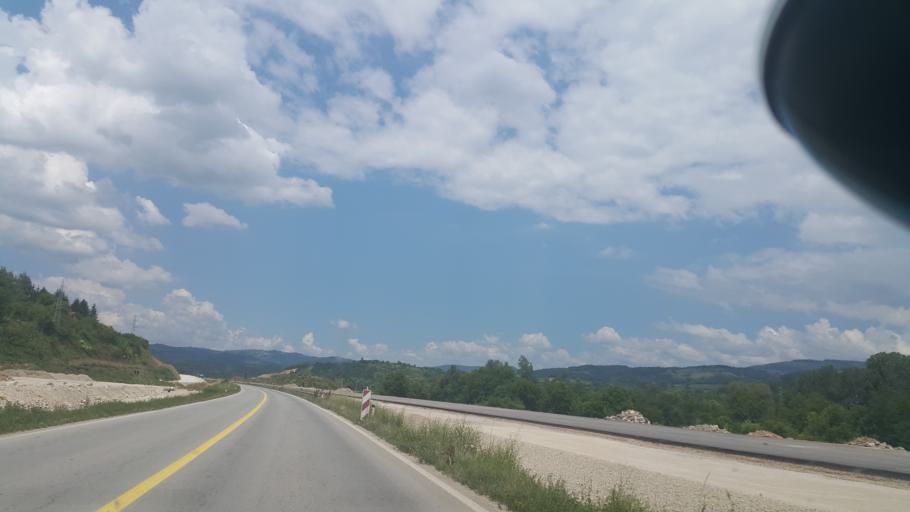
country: RS
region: Central Serbia
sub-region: Pirotski Okrug
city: Pirot
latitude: 43.2032
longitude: 22.5567
